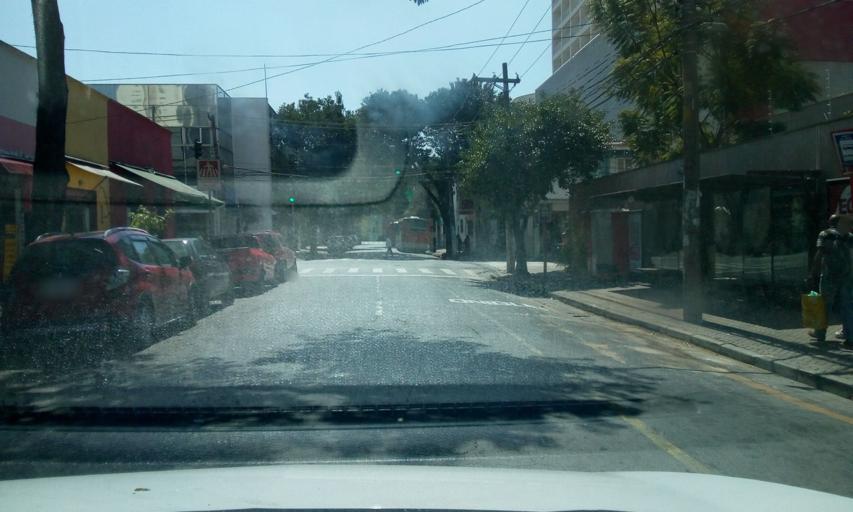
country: BR
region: Sao Paulo
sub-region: Sao Paulo
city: Sao Paulo
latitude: -23.5232
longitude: -46.6978
